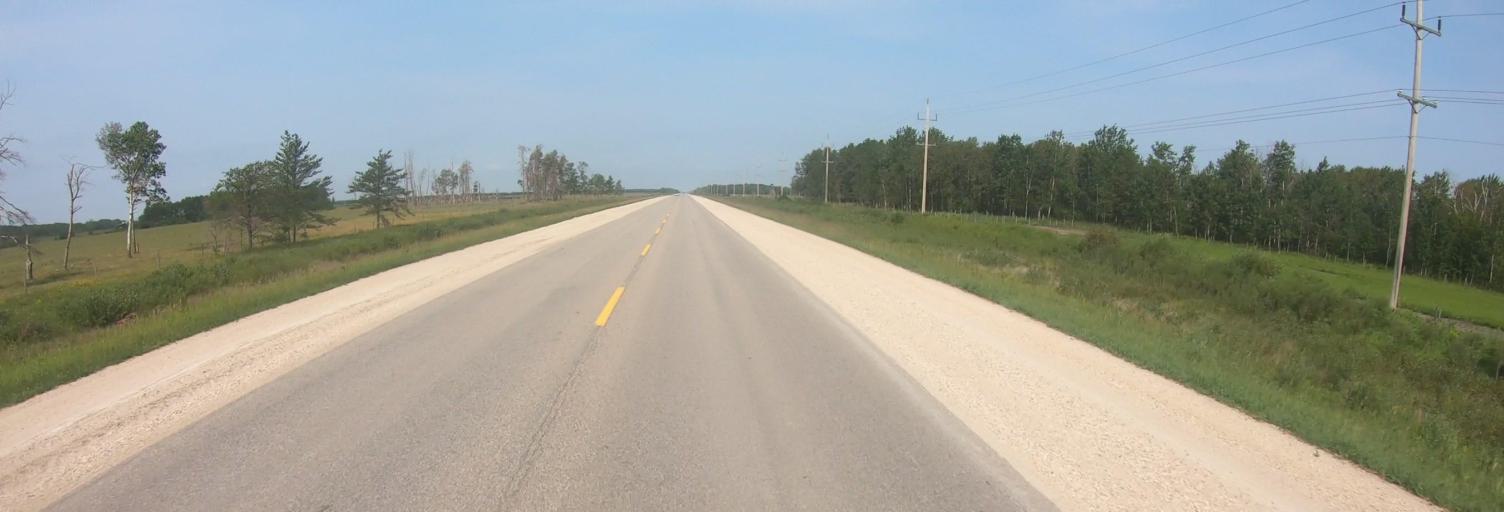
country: CA
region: Manitoba
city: La Broquerie
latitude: 49.3100
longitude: -96.5652
